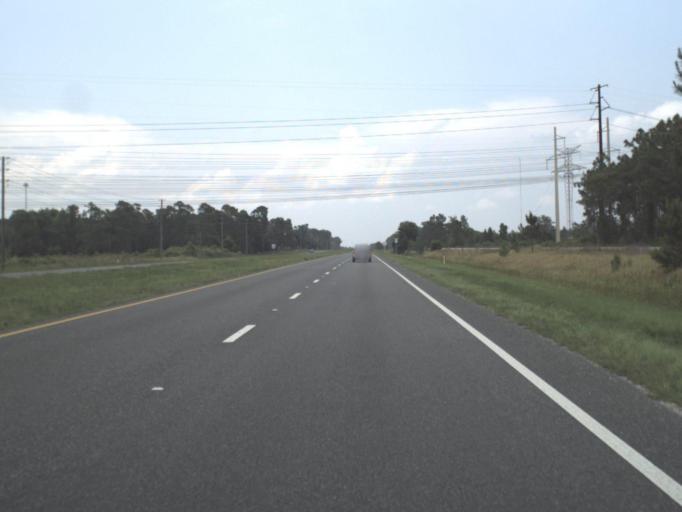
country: US
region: Florida
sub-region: Putnam County
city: Palatka
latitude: 29.7258
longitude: -81.6521
